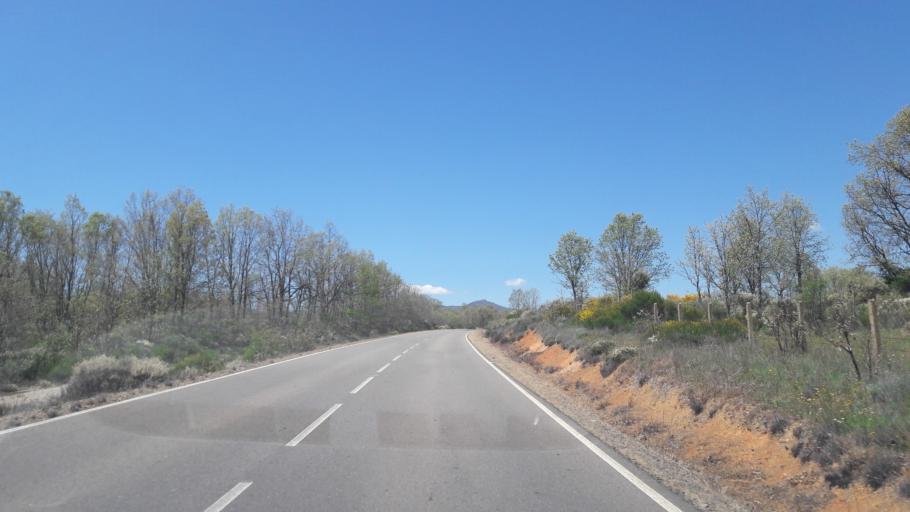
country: ES
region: Castille and Leon
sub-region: Provincia de Salamanca
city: Monleon
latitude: 40.5916
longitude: -5.8751
